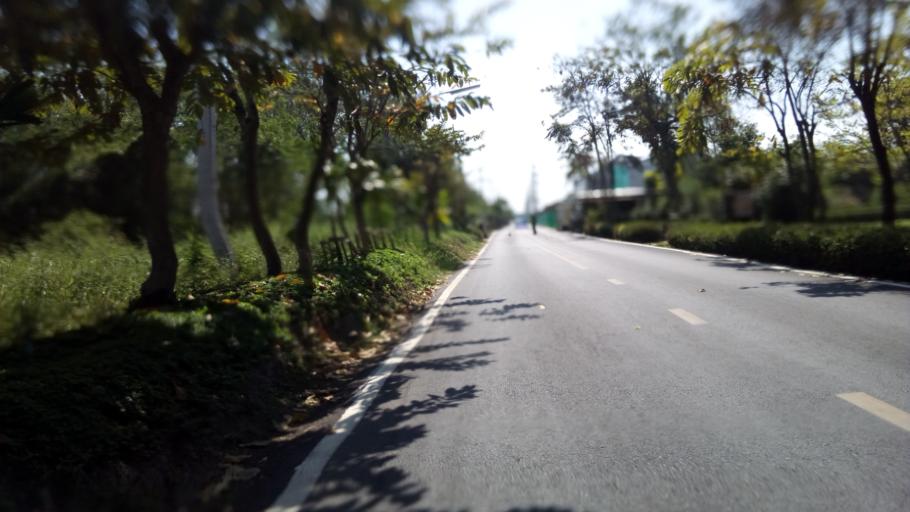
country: TH
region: Pathum Thani
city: Nong Suea
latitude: 14.0659
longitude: 100.8377
